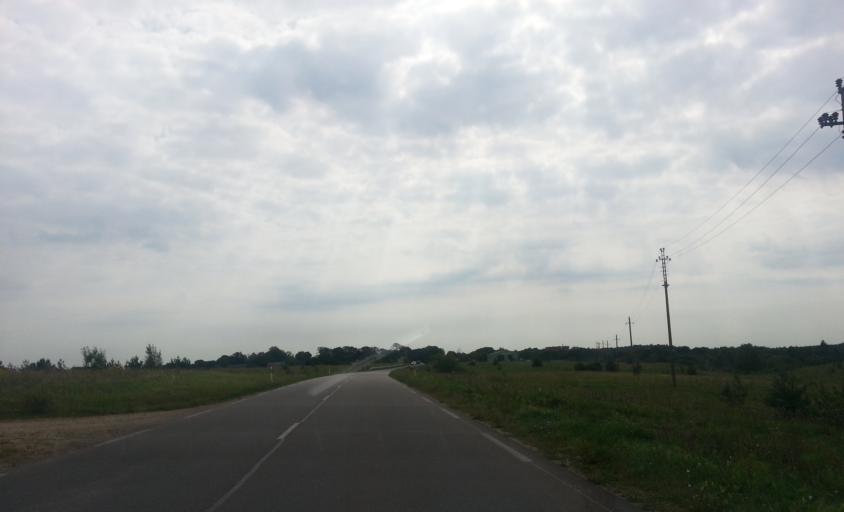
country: LT
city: Grigiskes
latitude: 54.7443
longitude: 25.0817
